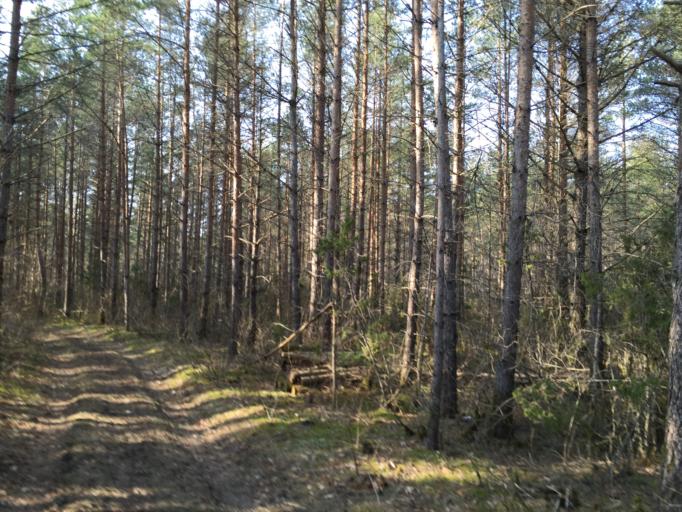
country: EE
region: Saare
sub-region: Orissaare vald
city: Orissaare
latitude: 58.5748
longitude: 23.2734
